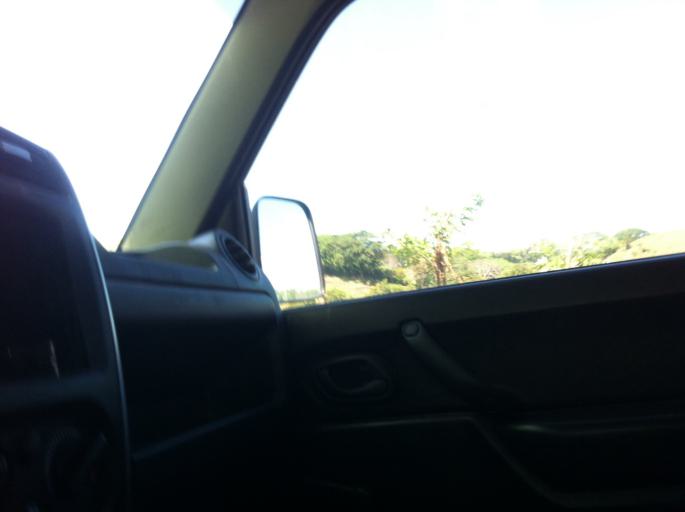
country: NI
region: Masaya
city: Niquinohomo
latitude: 11.9148
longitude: -86.0964
